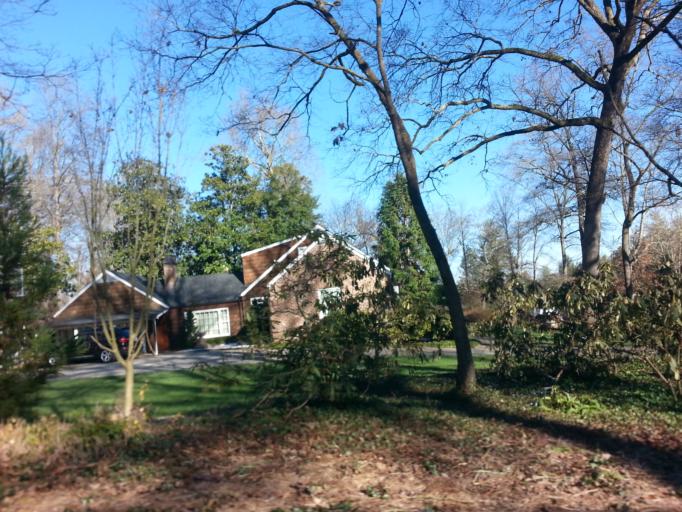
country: US
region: Tennessee
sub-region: Knox County
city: Knoxville
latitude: 35.9190
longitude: -84.0133
